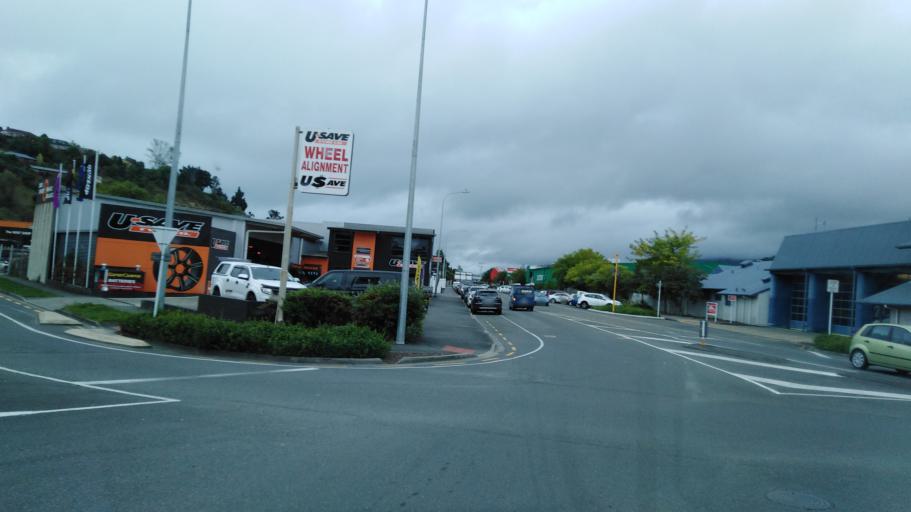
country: NZ
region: Nelson
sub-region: Nelson City
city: Nelson
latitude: -41.2739
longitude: 173.2760
